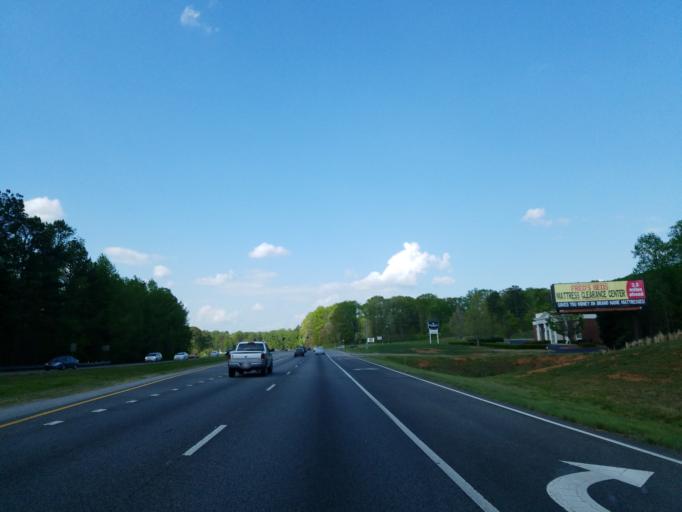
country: US
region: Georgia
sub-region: Forsyth County
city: Cumming
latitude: 34.2695
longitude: -84.0807
